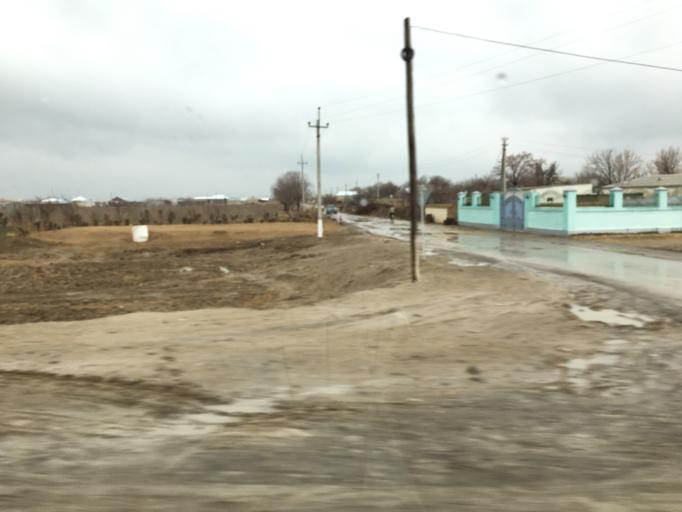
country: TM
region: Mary
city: Yoloeten
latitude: 37.2954
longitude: 62.3333
